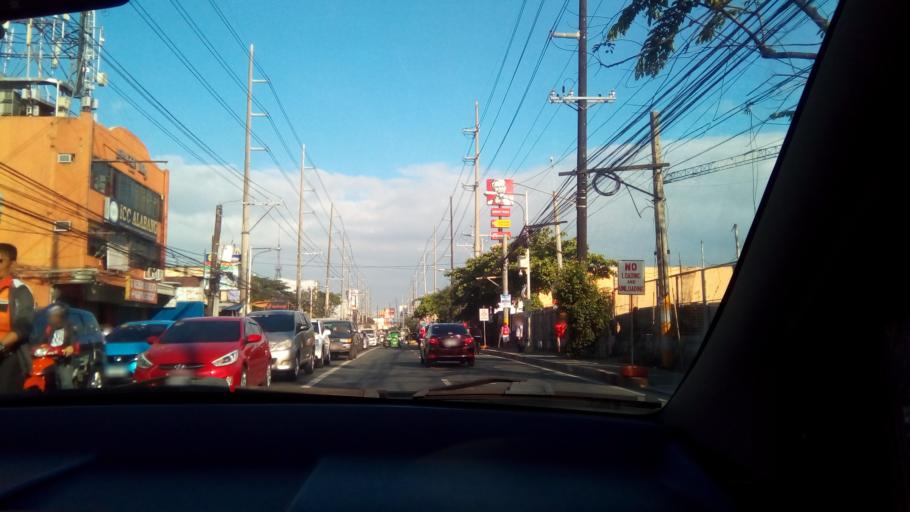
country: PH
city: Sambayanihan People's Village
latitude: 14.4319
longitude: 121.0149
